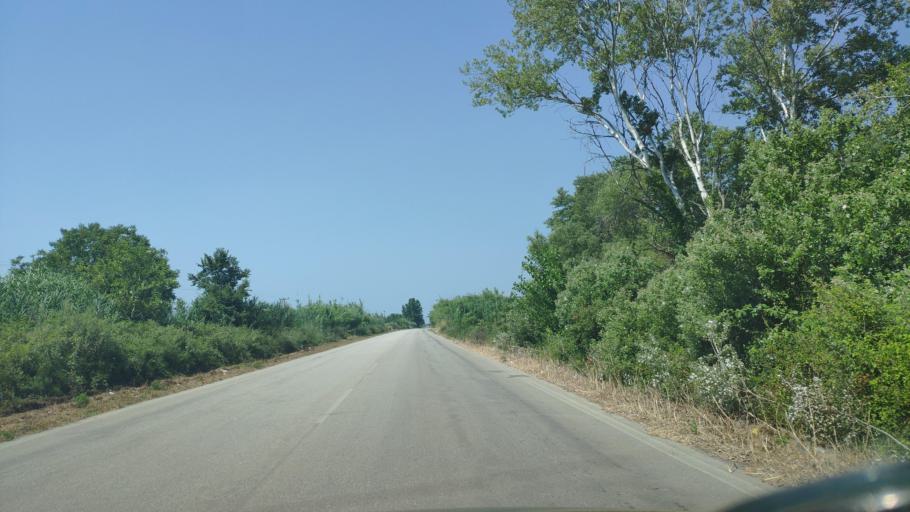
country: GR
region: Epirus
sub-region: Nomos Artas
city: Aneza
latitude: 39.1159
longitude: 20.9297
